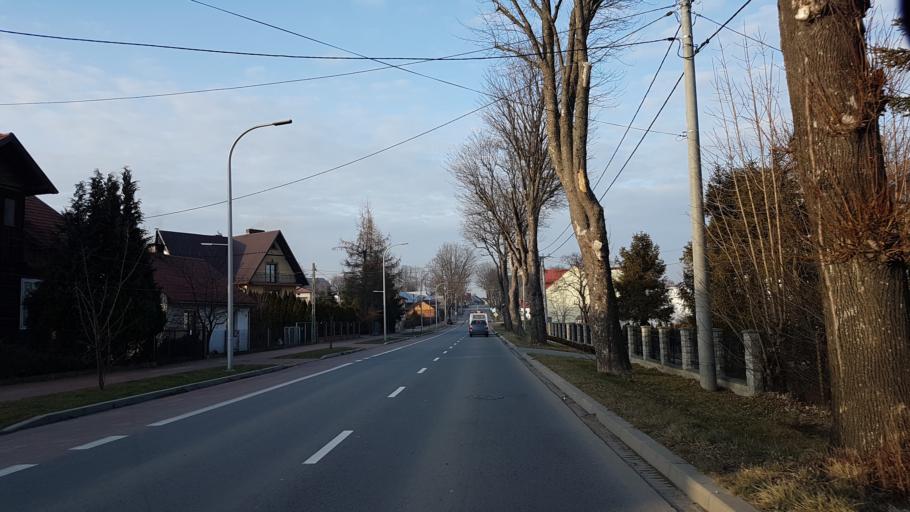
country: PL
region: Lesser Poland Voivodeship
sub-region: Powiat nowosadecki
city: Stary Sacz
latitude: 49.5540
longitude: 20.6392
